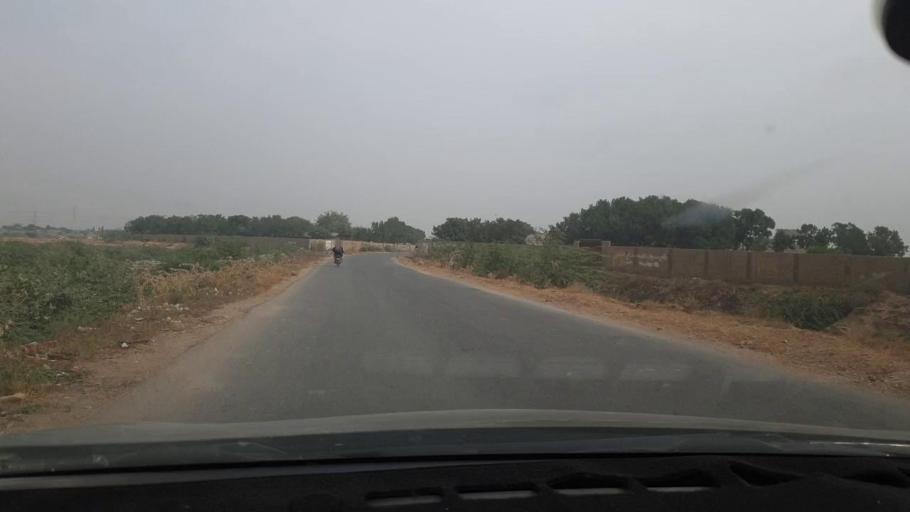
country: PK
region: Sindh
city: Malir Cantonment
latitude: 24.9141
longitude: 67.2688
